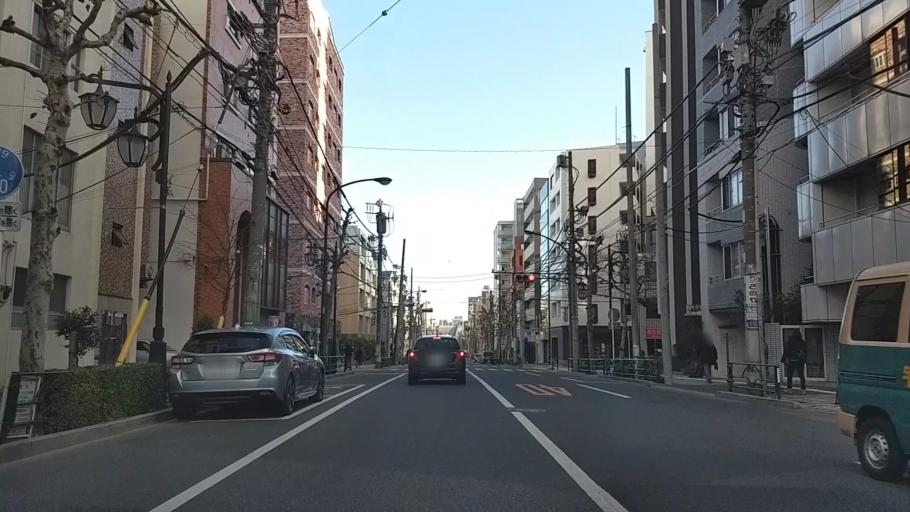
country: JP
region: Tokyo
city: Tokyo
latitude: 35.7290
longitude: 139.7316
